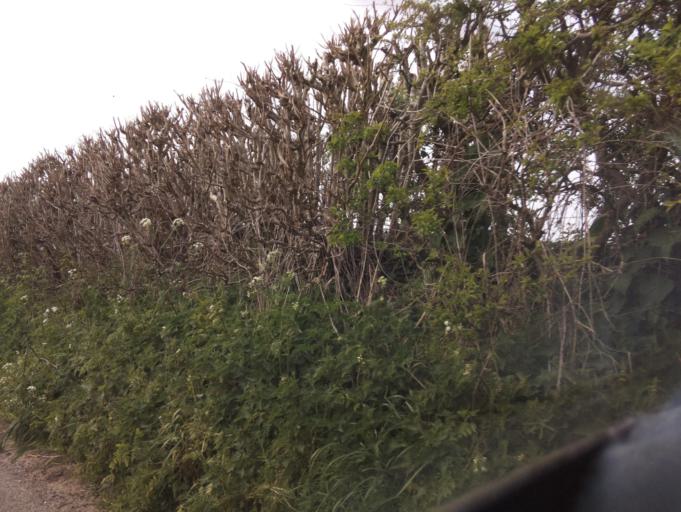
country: GB
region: England
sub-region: Dorset
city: Sherborne
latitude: 50.9712
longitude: -2.5093
